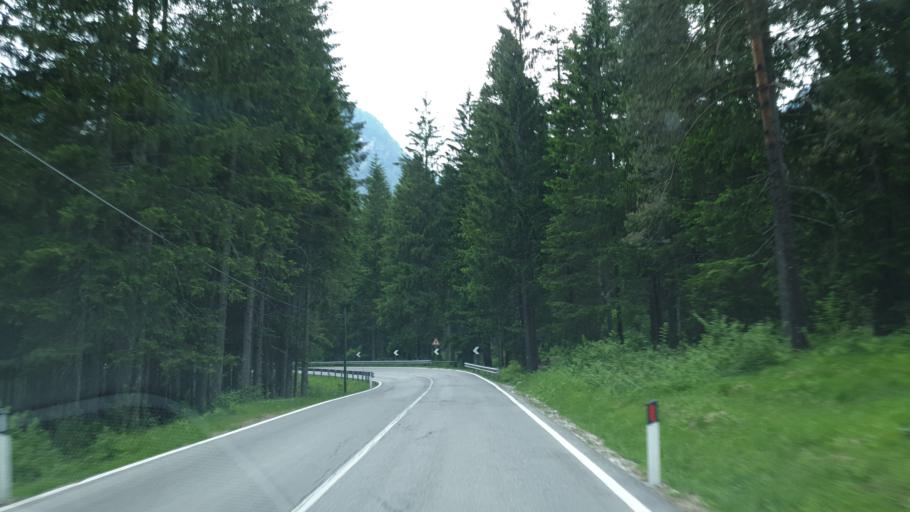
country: IT
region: Veneto
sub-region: Provincia di Belluno
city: Auronzo
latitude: 46.5776
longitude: 12.3684
